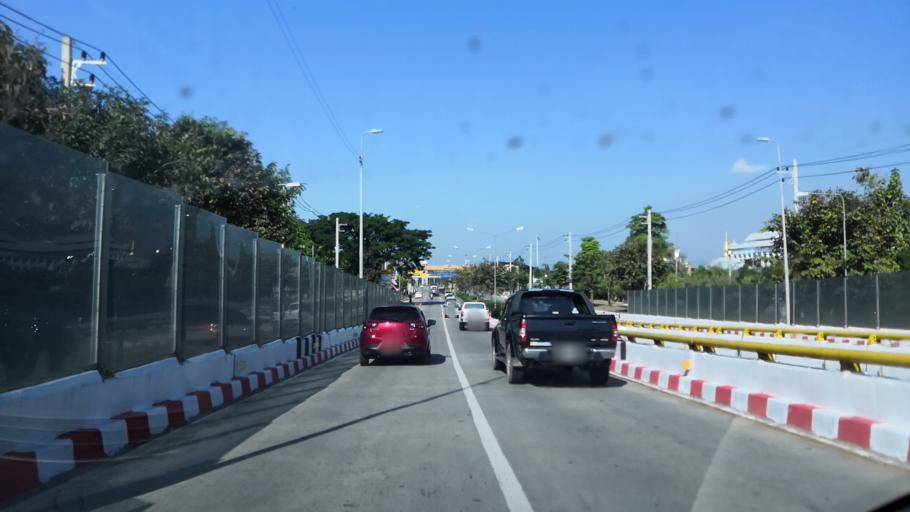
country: TH
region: Chiang Rai
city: Chiang Rai
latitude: 19.9257
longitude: 99.8625
